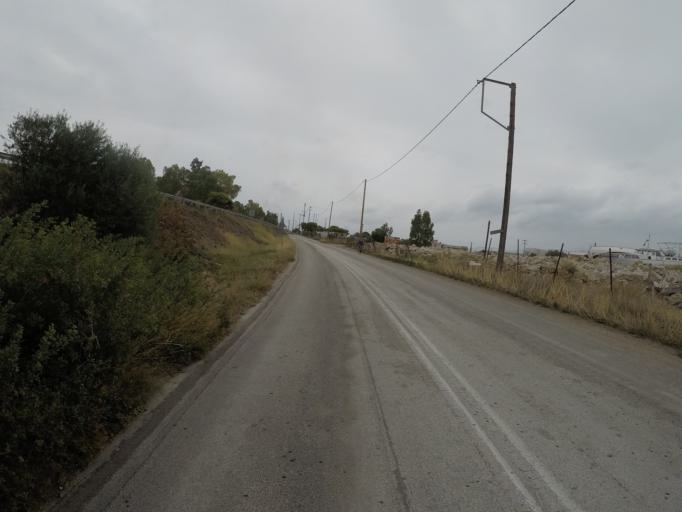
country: GR
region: Peloponnese
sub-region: Nomos Korinthias
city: Isthmia
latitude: 37.9199
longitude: 23.0583
